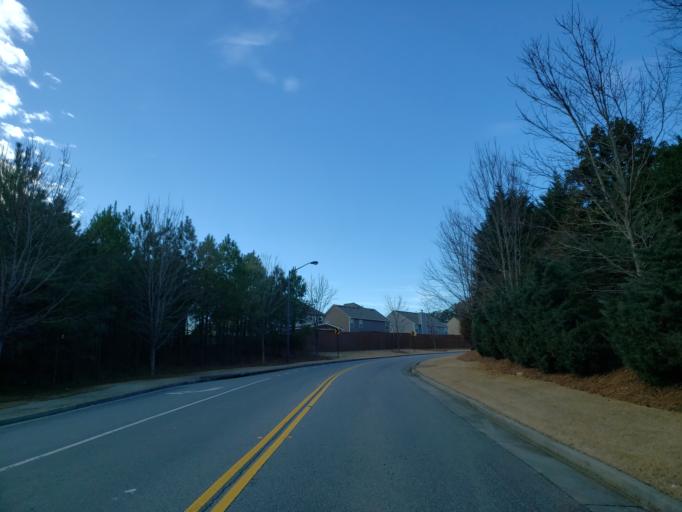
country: US
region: Georgia
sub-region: Cobb County
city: Kennesaw
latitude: 34.0615
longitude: -84.6100
